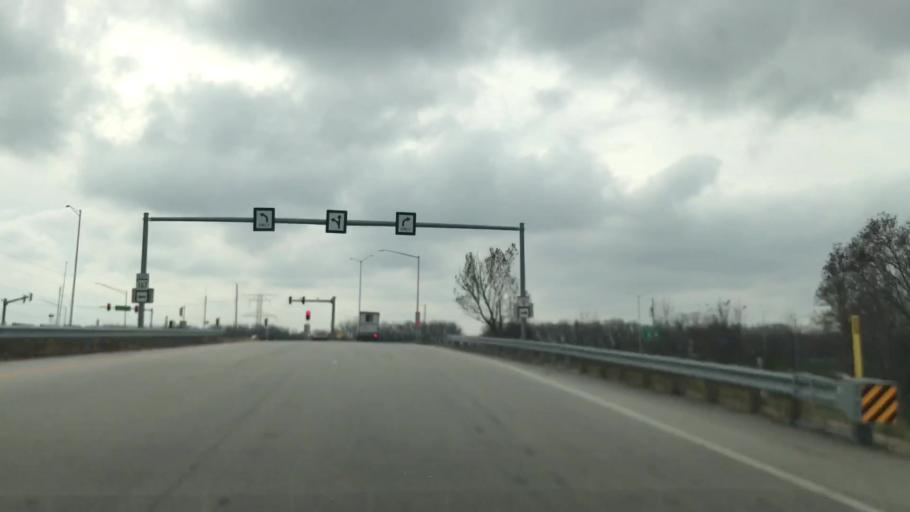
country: US
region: Wisconsin
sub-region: Washington County
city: Germantown
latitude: 43.2142
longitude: -88.1496
